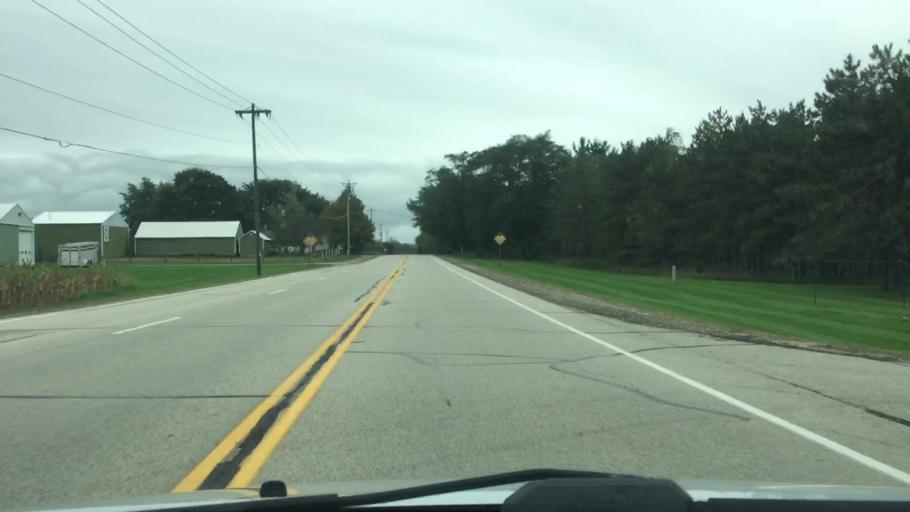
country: US
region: Wisconsin
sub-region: Jefferson County
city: Palmyra
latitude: 42.7779
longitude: -88.5544
